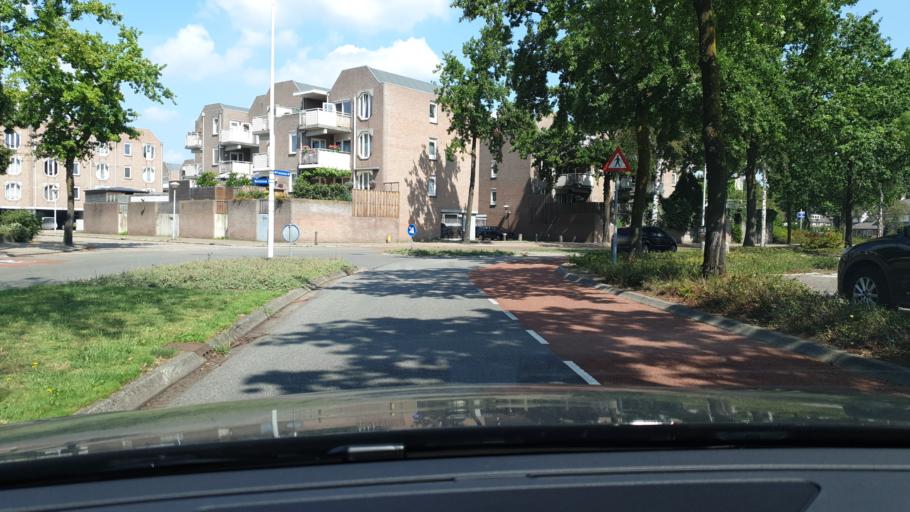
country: NL
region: North Brabant
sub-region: Gemeente Eindhoven
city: Eindhoven
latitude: 51.4818
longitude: 5.4496
